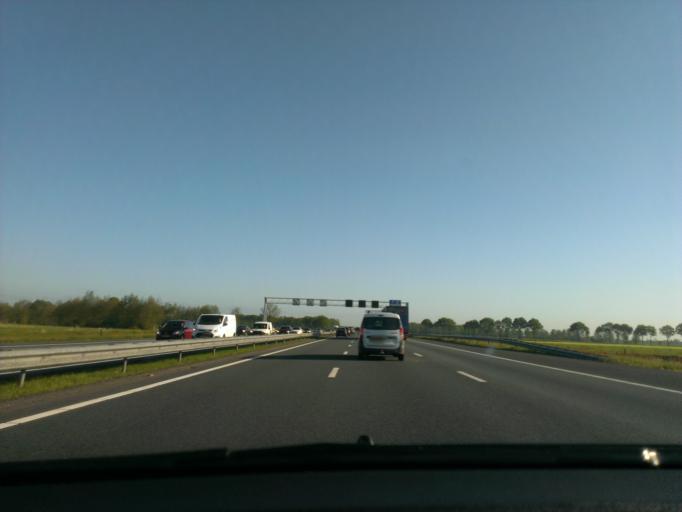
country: NL
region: Overijssel
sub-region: Gemeente Staphorst
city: Staphorst
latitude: 52.6121
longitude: 6.2074
